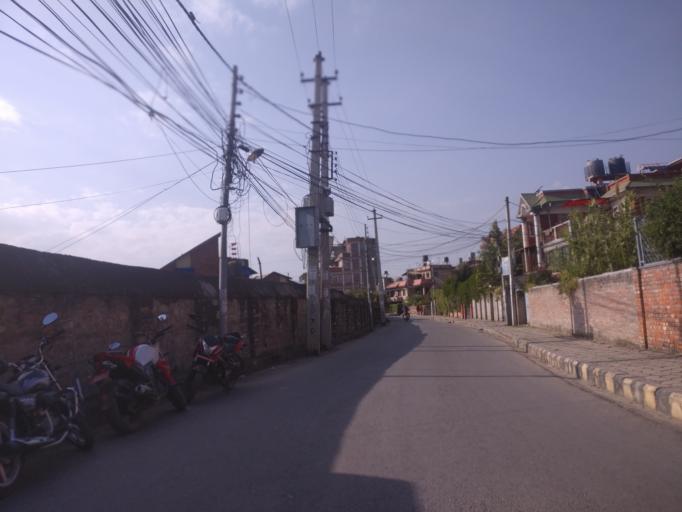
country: NP
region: Central Region
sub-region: Bagmati Zone
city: Patan
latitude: 27.6832
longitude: 85.3252
